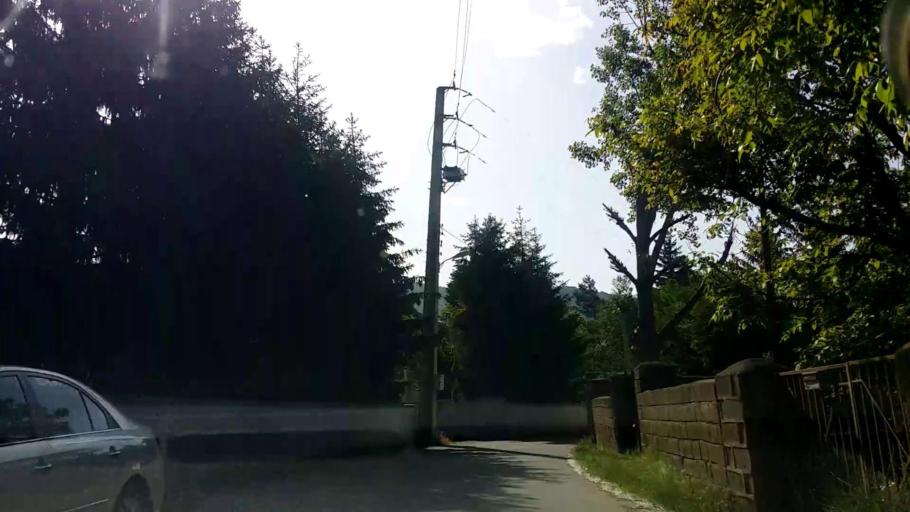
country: IR
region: Mazandaran
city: `Abbasabad
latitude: 36.5284
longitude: 51.1776
